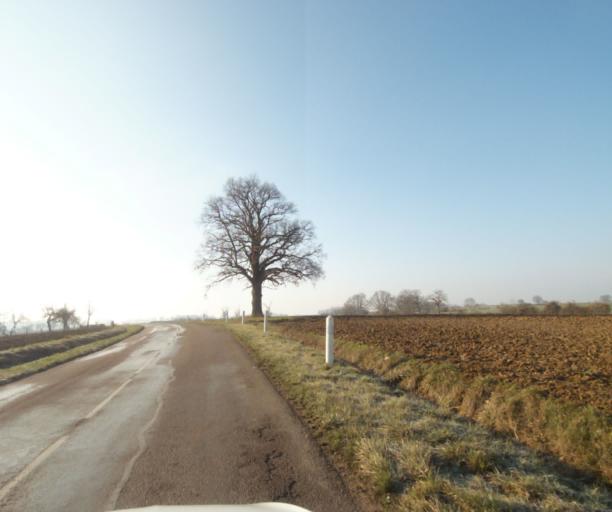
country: FR
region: Champagne-Ardenne
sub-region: Departement de la Haute-Marne
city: Montier-en-Der
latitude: 48.4428
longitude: 4.7581
